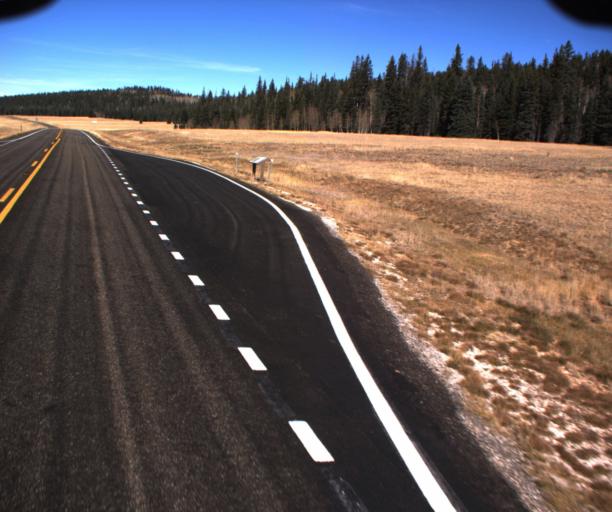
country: US
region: Arizona
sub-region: Coconino County
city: Grand Canyon
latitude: 36.3559
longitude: -112.1185
